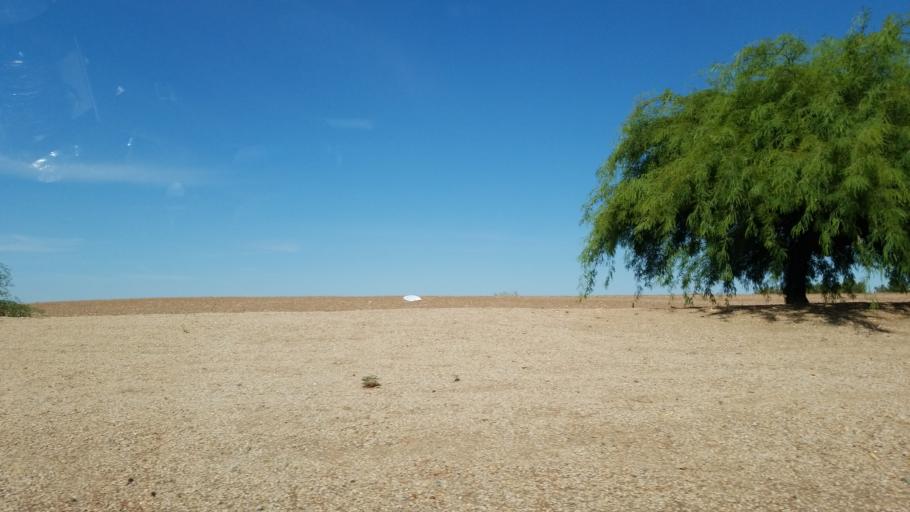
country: US
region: Arizona
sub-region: Maricopa County
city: Glendale
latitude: 33.6092
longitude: -112.1514
